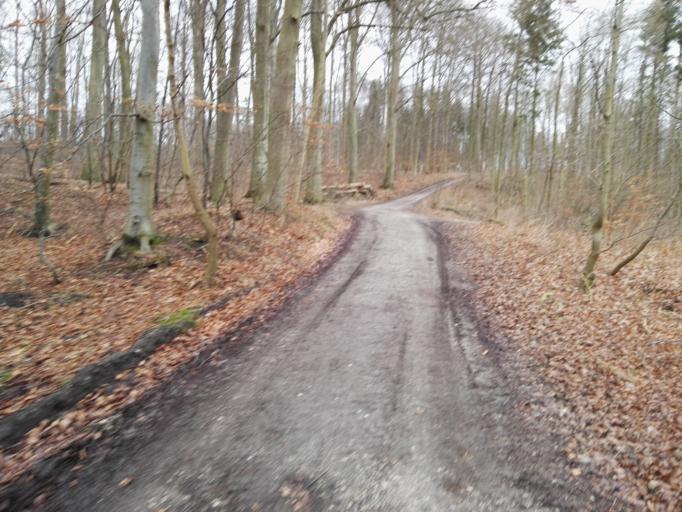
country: DK
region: Zealand
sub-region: Lejre Kommune
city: Lejre
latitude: 55.6405
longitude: 11.9179
